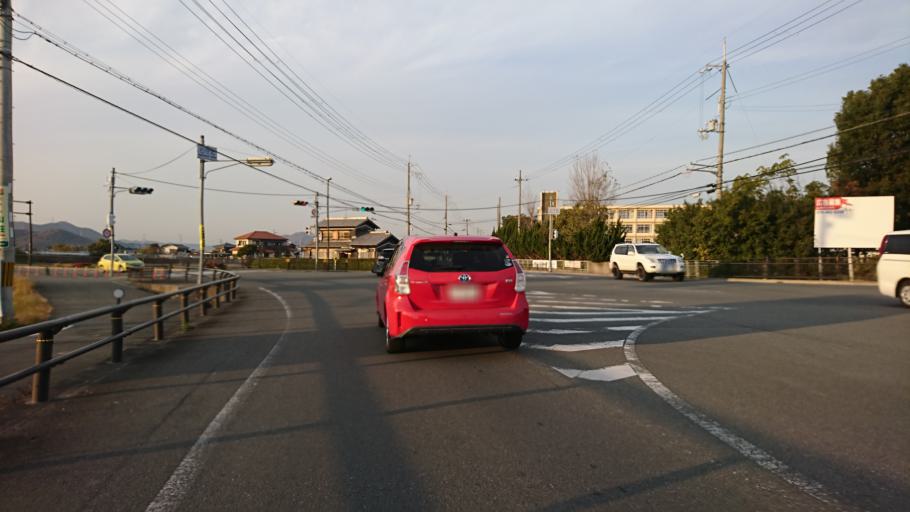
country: JP
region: Hyogo
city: Kakogawacho-honmachi
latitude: 34.7748
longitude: 134.8767
